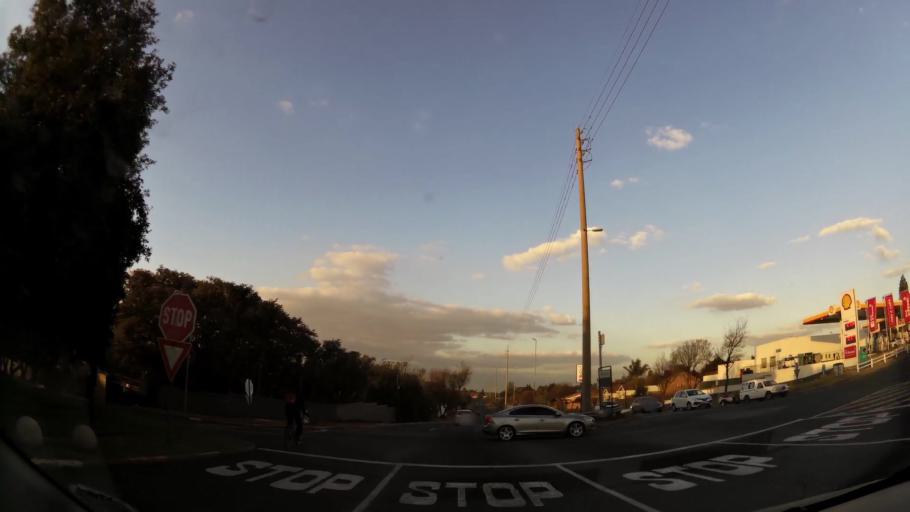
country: ZA
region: Gauteng
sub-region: West Rand District Municipality
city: Krugersdorp
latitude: -26.0774
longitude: 27.7787
